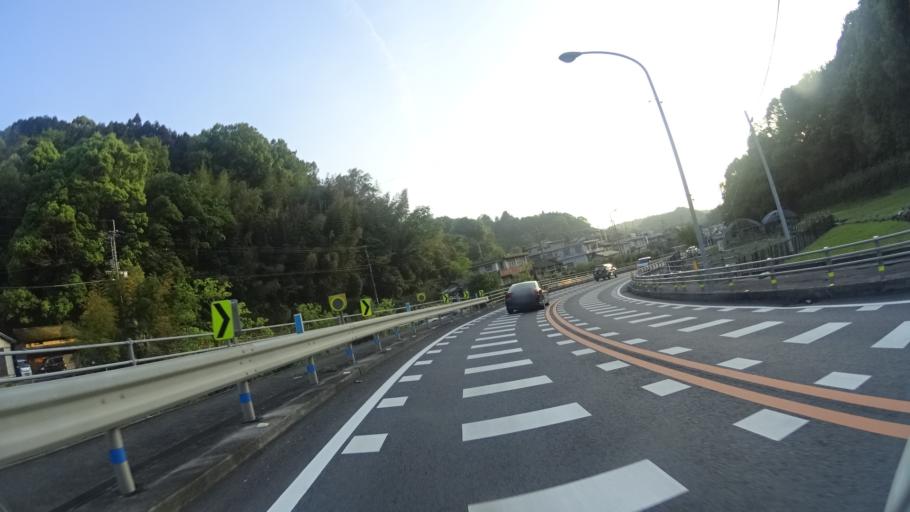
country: JP
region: Ehime
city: Kawanoecho
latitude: 33.9903
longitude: 133.6390
